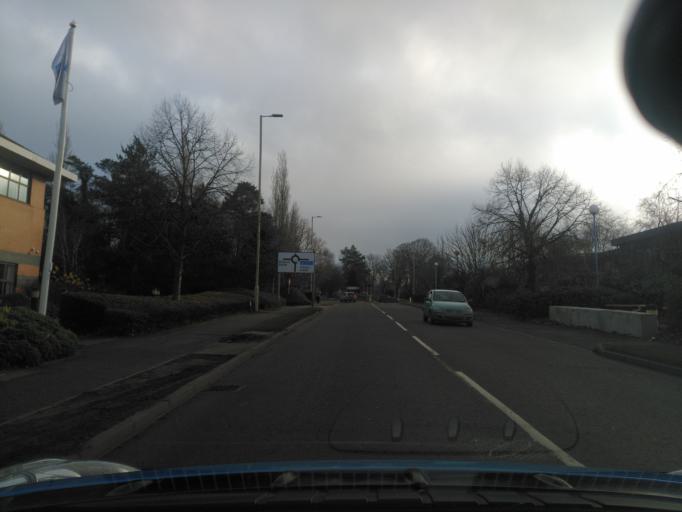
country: GB
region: England
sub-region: Hertfordshire
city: Letchworth Garden City
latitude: 51.9791
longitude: -0.2070
